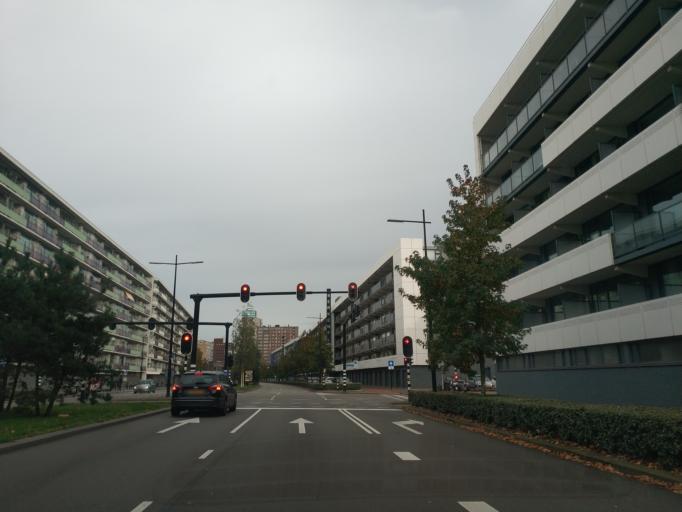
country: NL
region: North Brabant
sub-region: Gemeente Tilburg
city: Tilburg
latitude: 51.5603
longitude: 5.0676
